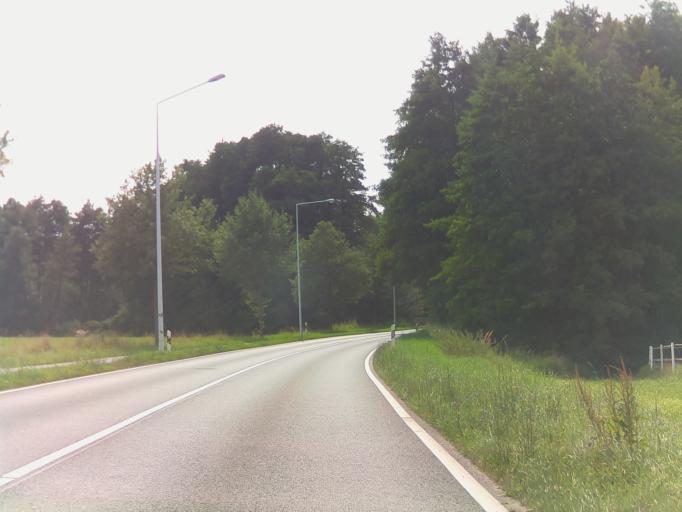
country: DE
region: Hesse
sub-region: Regierungsbezirk Darmstadt
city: Darmstadt
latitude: 49.8972
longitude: 8.6914
